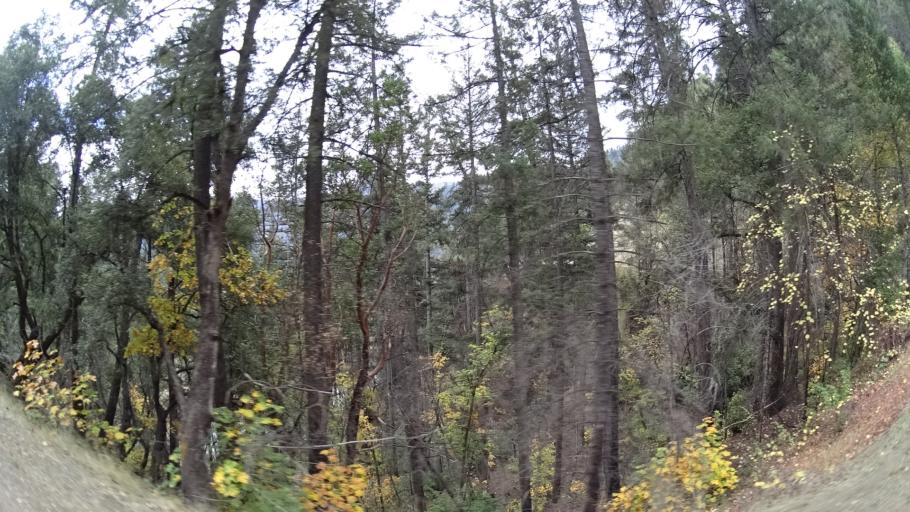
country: US
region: California
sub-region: Siskiyou County
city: Happy Camp
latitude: 41.7760
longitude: -123.3490
